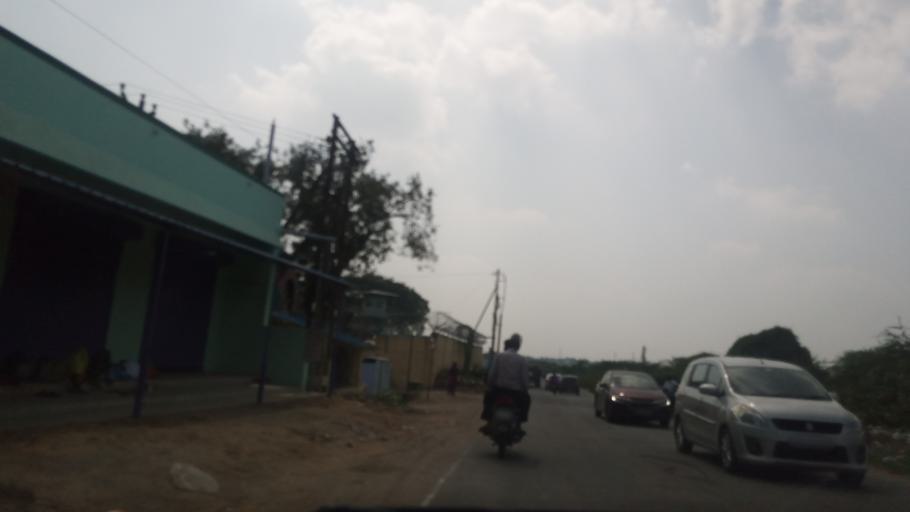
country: IN
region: Tamil Nadu
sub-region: Vellore
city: Arakkonam
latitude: 13.0541
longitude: 79.6742
